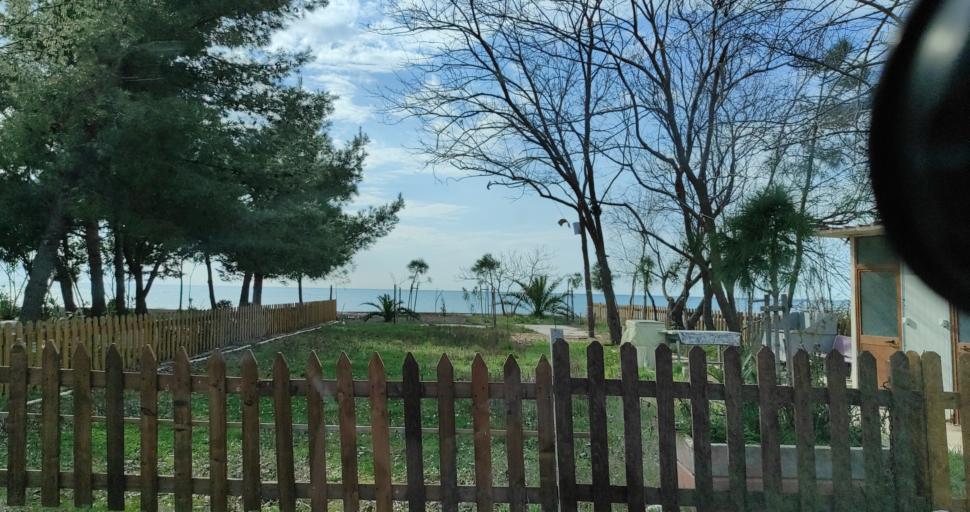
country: AL
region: Lezhe
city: Shengjin
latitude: 41.7842
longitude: 19.6032
